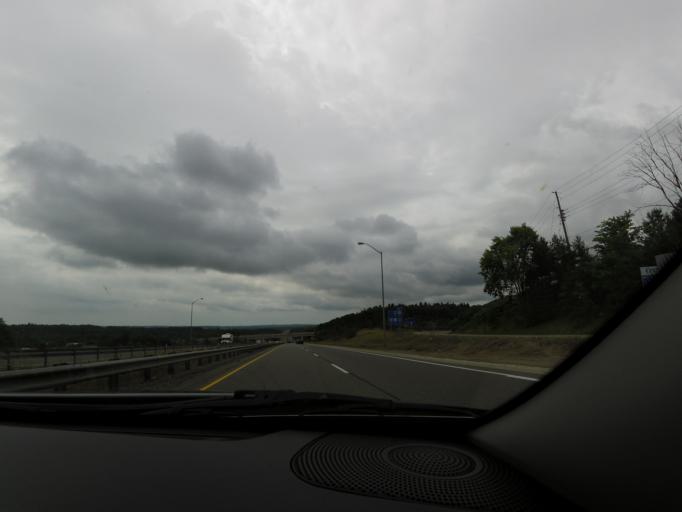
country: CA
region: Ontario
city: Orillia
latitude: 44.5924
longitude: -79.4467
